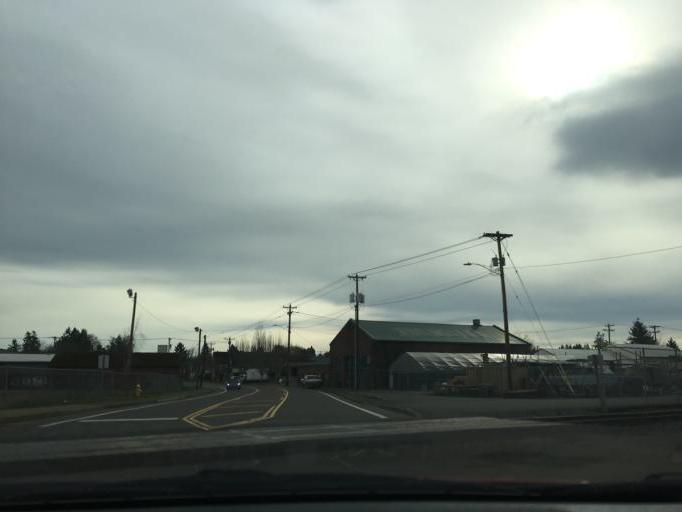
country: US
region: Oregon
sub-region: Marion County
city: Woodburn
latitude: 45.1422
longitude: -122.8567
